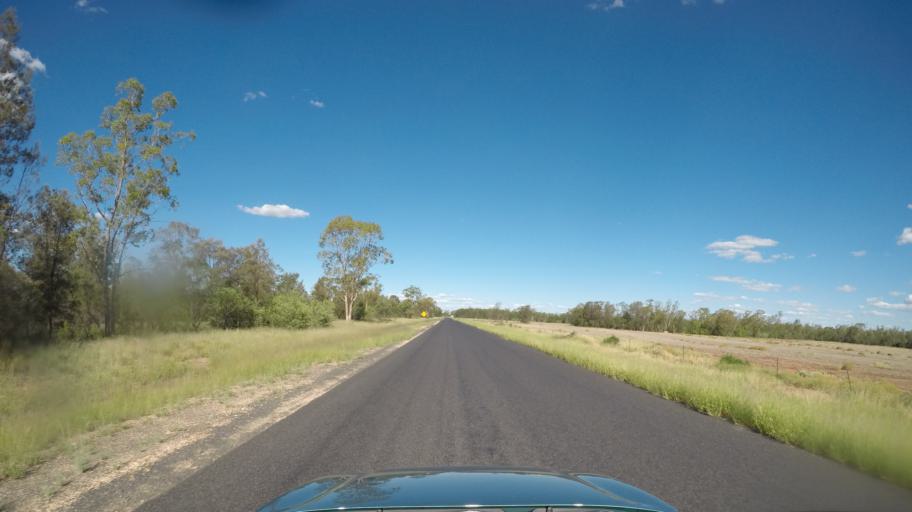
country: AU
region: Queensland
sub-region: Goondiwindi
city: Goondiwindi
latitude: -28.1700
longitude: 150.4685
